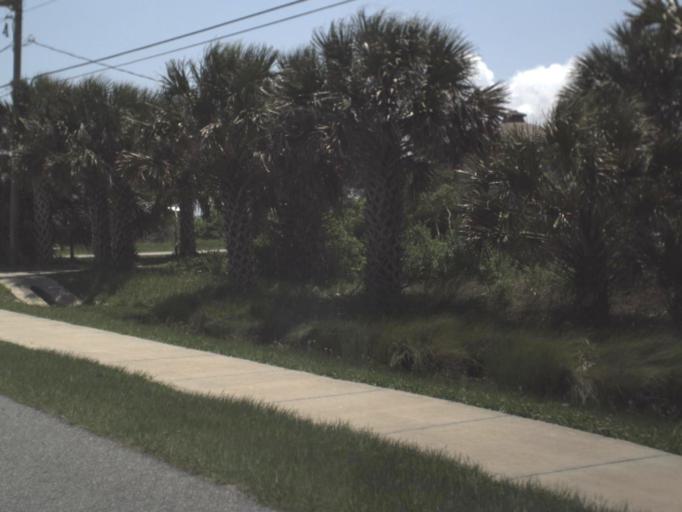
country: US
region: Florida
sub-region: Saint Johns County
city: Butler Beach
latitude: 29.7465
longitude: -81.2452
